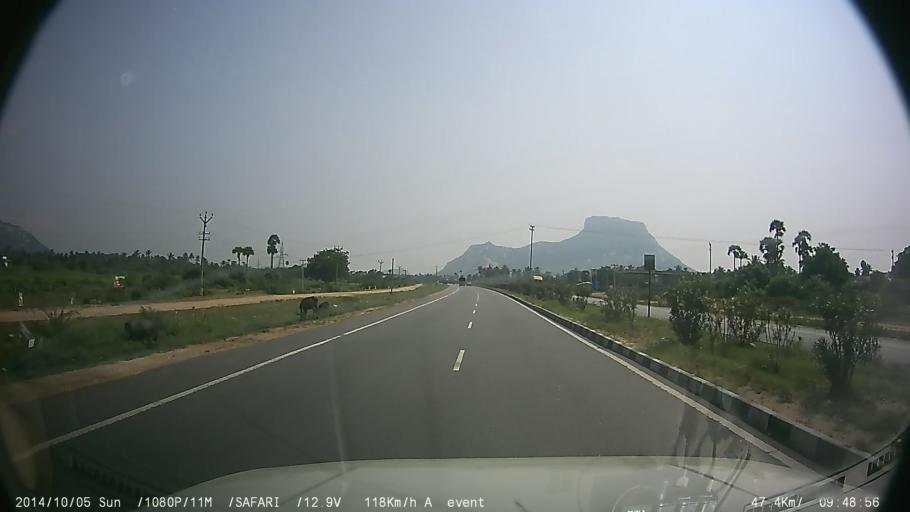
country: IN
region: Tamil Nadu
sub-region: Namakkal
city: Tiruchengode
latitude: 11.4716
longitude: 77.8281
